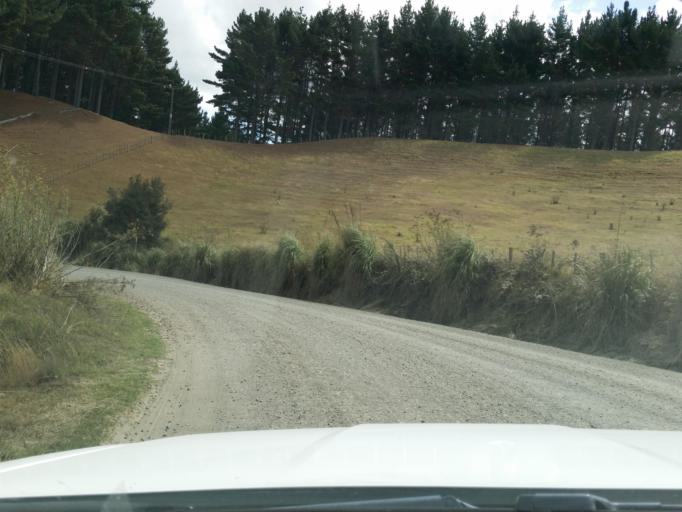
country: NZ
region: Auckland
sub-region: Auckland
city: Wellsford
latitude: -36.3003
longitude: 174.1106
